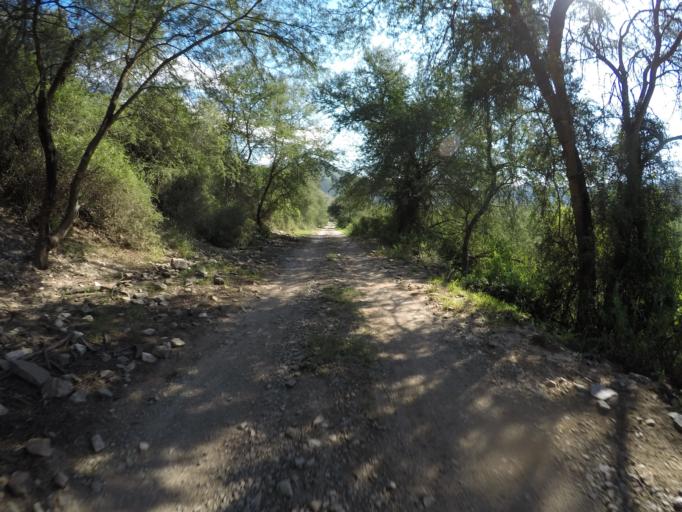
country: ZA
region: Eastern Cape
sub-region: Cacadu District Municipality
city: Kareedouw
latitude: -33.6651
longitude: 24.3727
